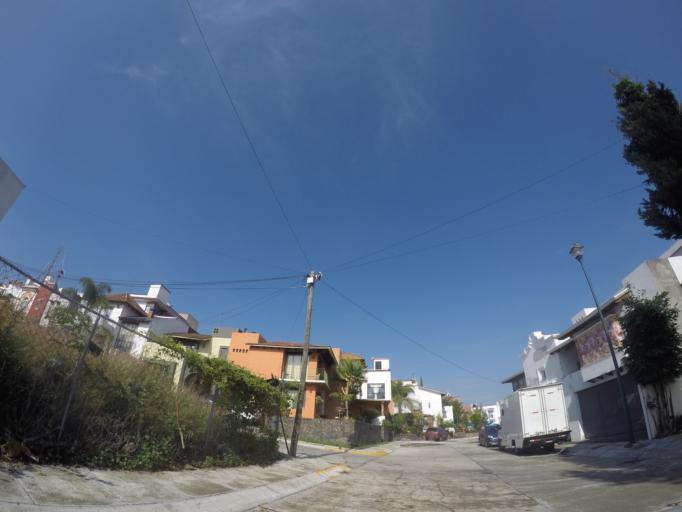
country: MX
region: Michoacan
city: Morelia
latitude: 19.6785
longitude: -101.2136
